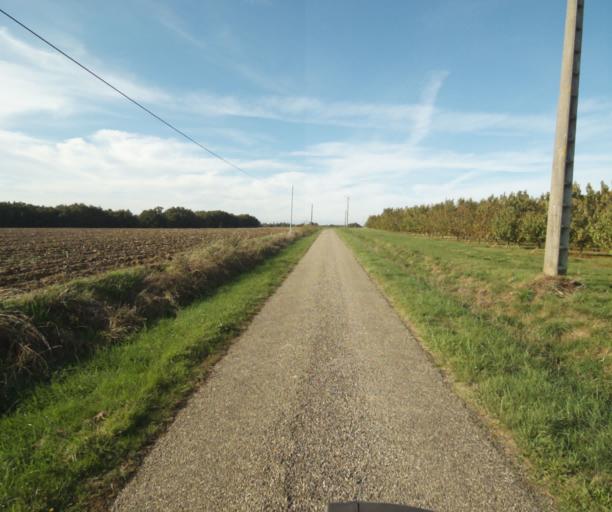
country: FR
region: Midi-Pyrenees
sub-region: Departement du Tarn-et-Garonne
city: Finhan
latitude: 43.9206
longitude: 1.1264
